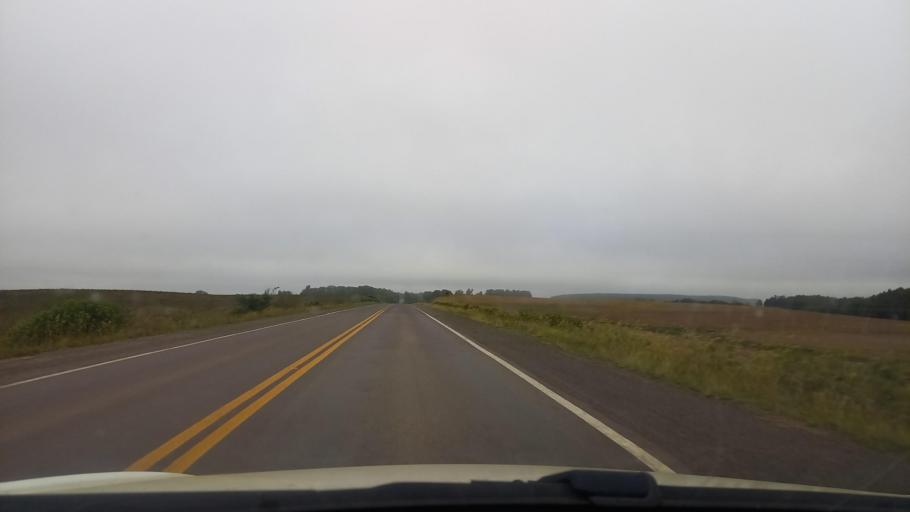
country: BR
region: Rio Grande do Sul
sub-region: Rosario Do Sul
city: Rosario do Sul
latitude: -30.1486
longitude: -54.6765
